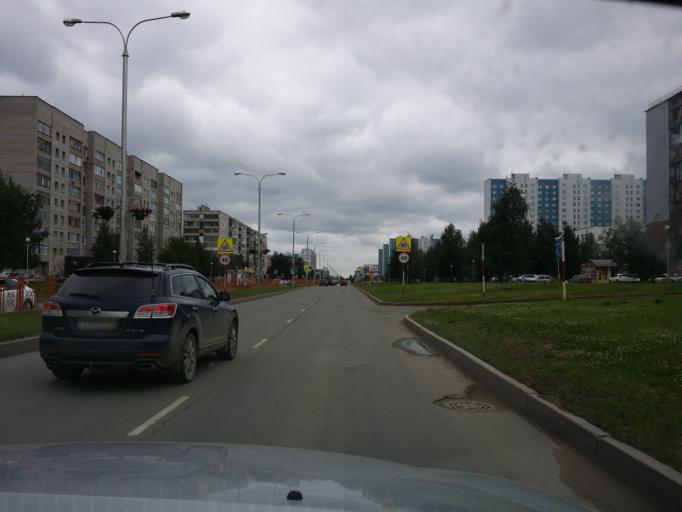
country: RU
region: Khanty-Mansiyskiy Avtonomnyy Okrug
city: Nizhnevartovsk
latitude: 60.9441
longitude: 76.6004
